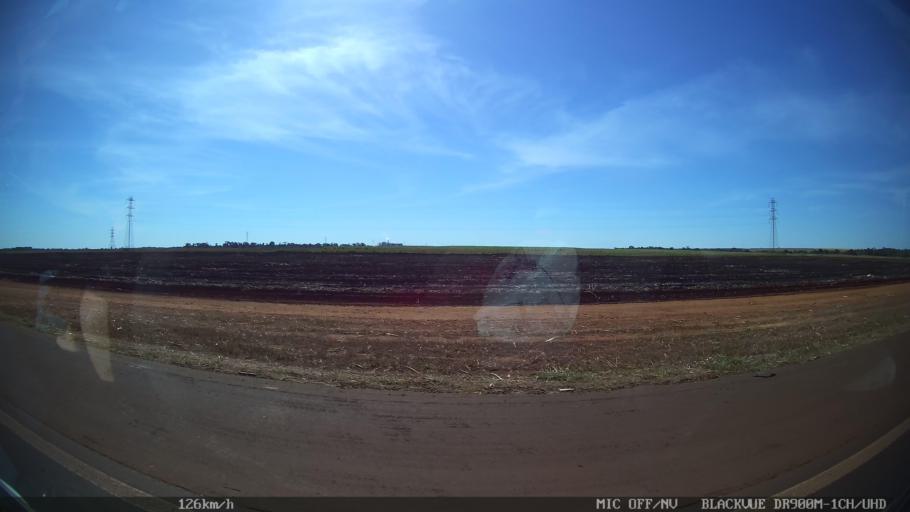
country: BR
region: Sao Paulo
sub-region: Guaira
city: Guaira
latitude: -20.4466
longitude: -48.2098
